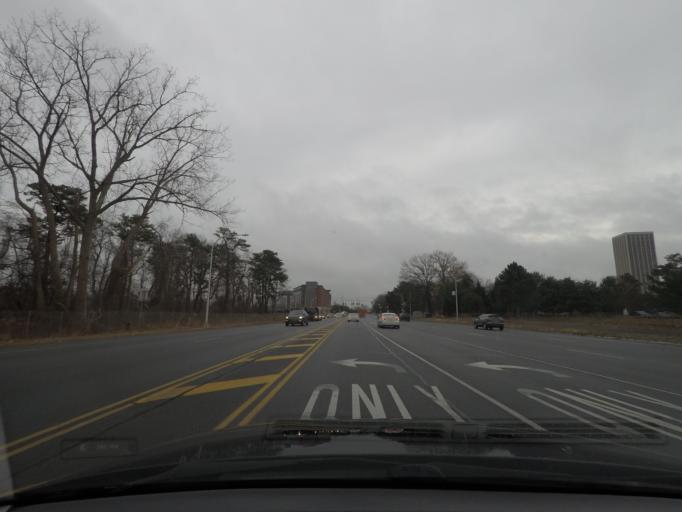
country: US
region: New York
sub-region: Albany County
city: Roessleville
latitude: 42.6919
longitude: -73.8256
